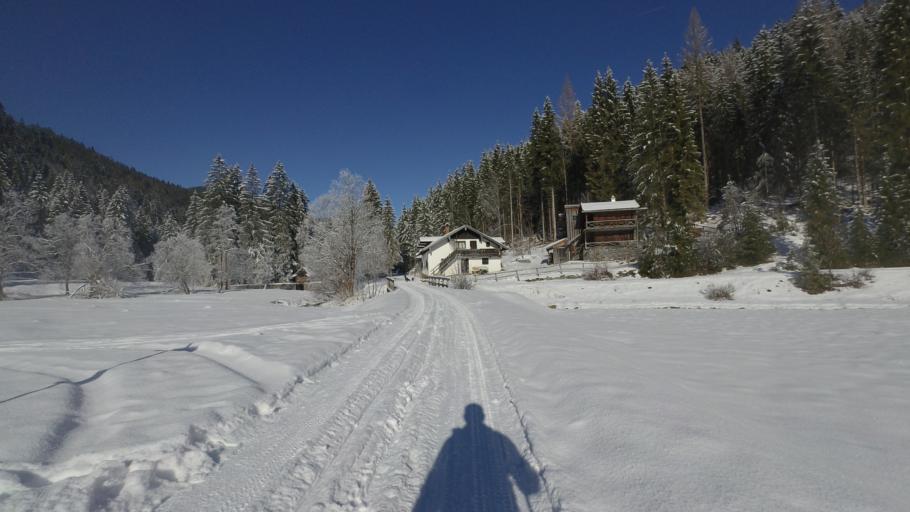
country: DE
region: Bavaria
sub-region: Upper Bavaria
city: Unterwossen
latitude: 47.7158
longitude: 12.5533
